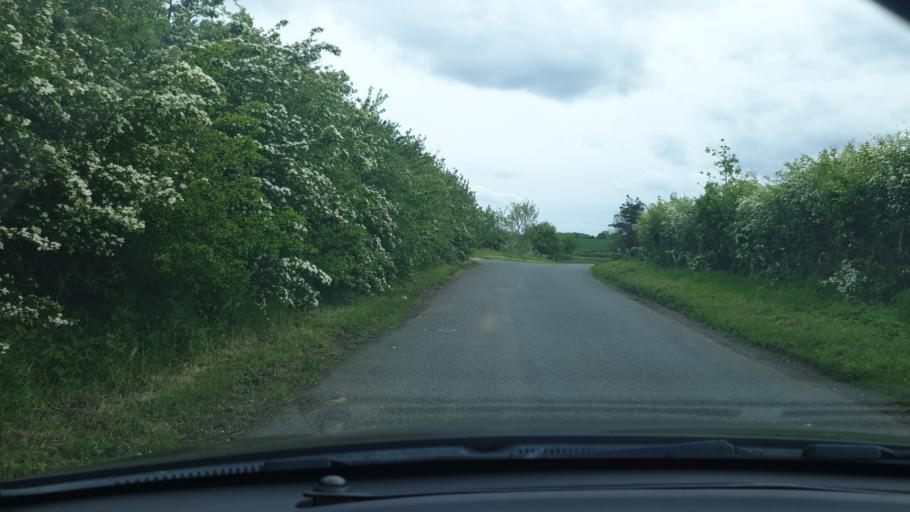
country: GB
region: England
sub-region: Essex
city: Mistley
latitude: 51.9157
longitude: 1.1627
